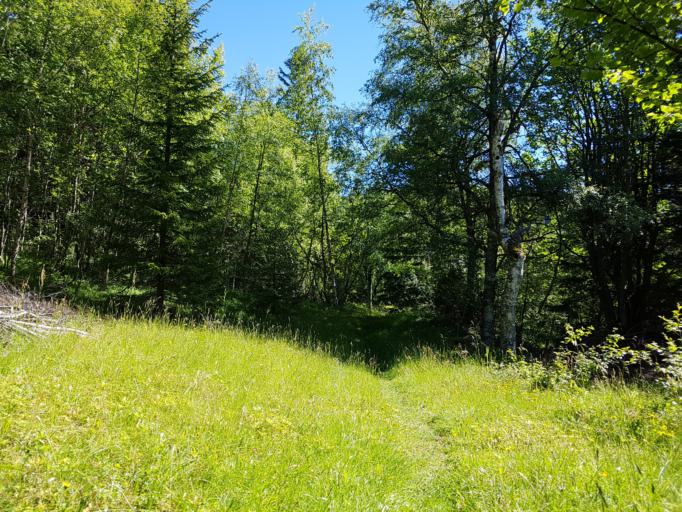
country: NO
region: Sor-Trondelag
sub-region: Skaun
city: Borsa
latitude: 63.4315
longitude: 10.1938
